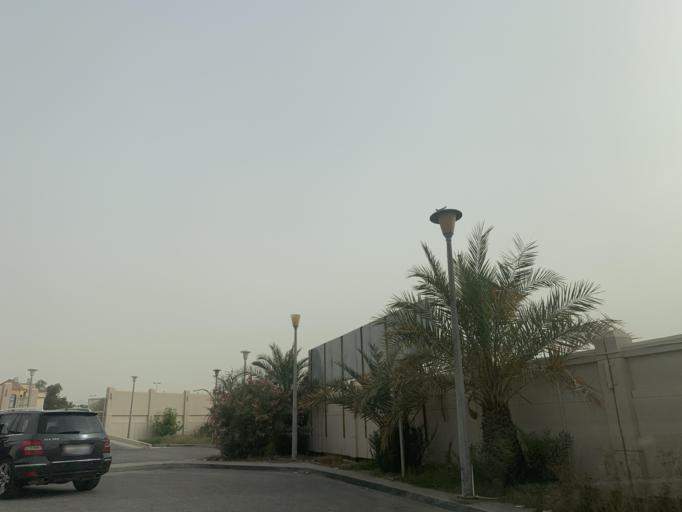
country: BH
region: Northern
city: Madinat `Isa
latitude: 26.1560
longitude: 50.5753
